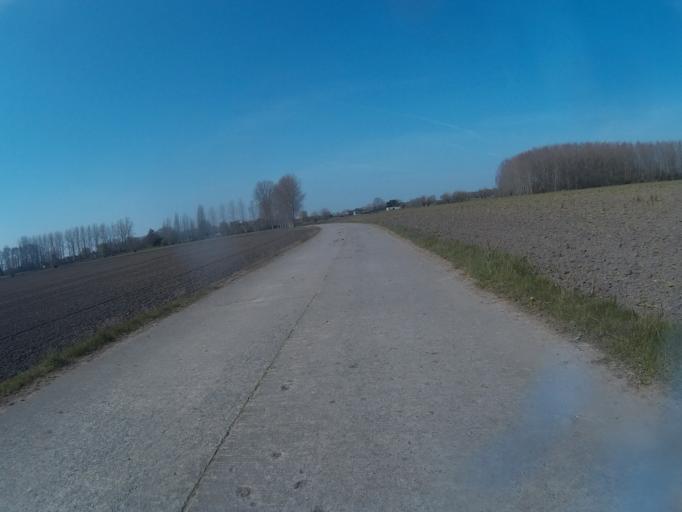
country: BE
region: Flanders
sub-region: Provincie Oost-Vlaanderen
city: Aalter
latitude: 51.1228
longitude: 3.4489
